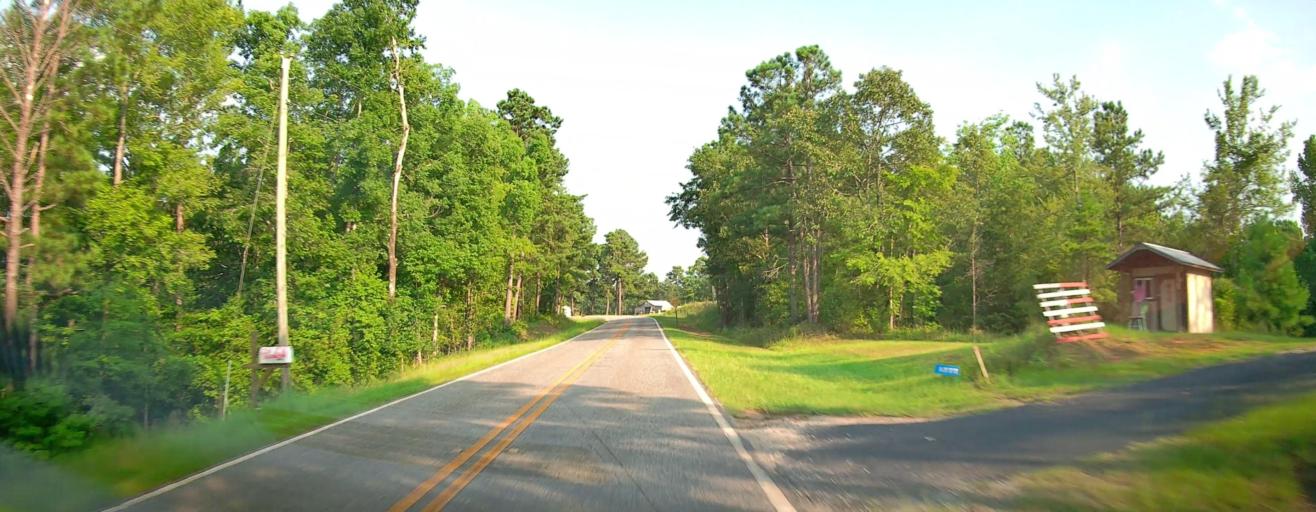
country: US
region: Georgia
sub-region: Monroe County
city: Forsyth
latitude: 33.0948
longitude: -83.7537
